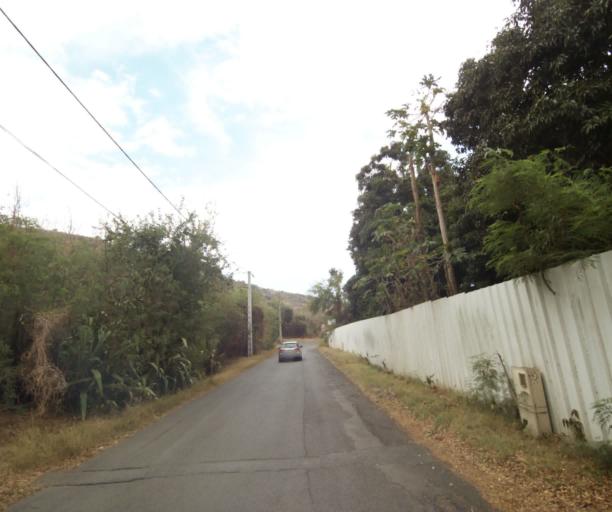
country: RE
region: Reunion
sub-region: Reunion
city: Saint-Paul
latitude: -21.0018
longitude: 55.3011
